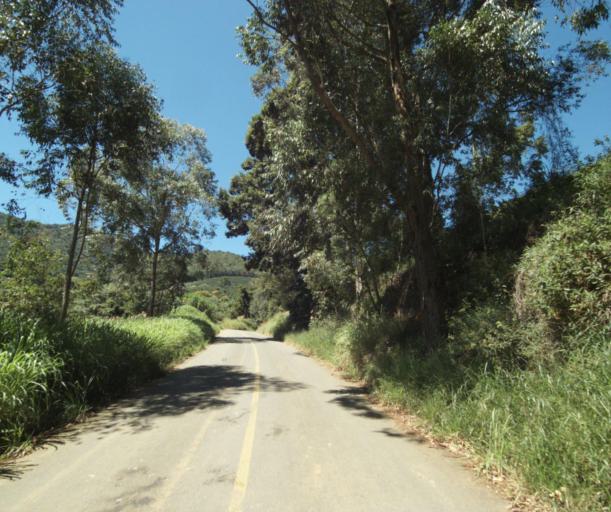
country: BR
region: Minas Gerais
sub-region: Espera Feliz
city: Espera Feliz
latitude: -20.6063
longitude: -41.8335
